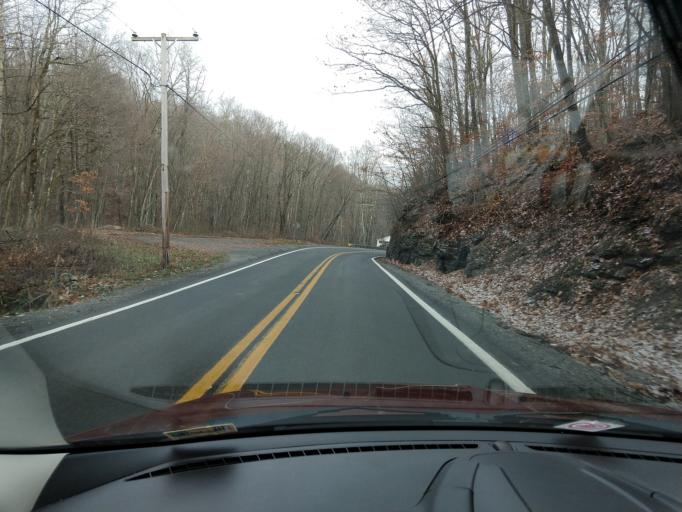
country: US
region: West Virginia
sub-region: Greenbrier County
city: Rainelle
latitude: 38.0670
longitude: -80.7082
